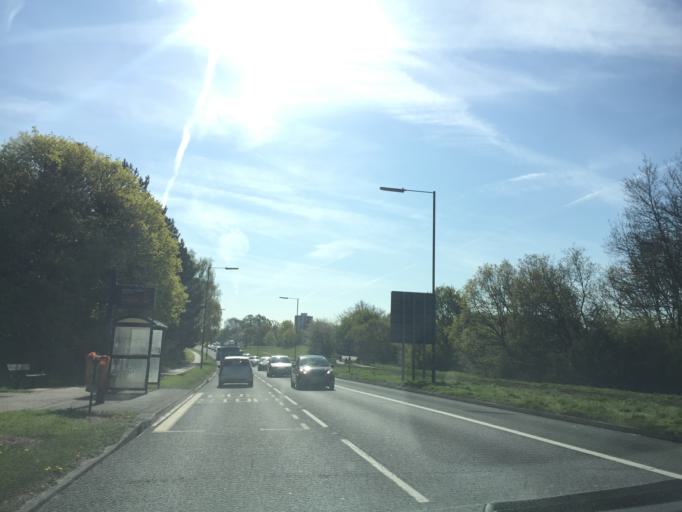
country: GB
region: England
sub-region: Essex
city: Harlow
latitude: 51.7668
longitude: 0.1012
